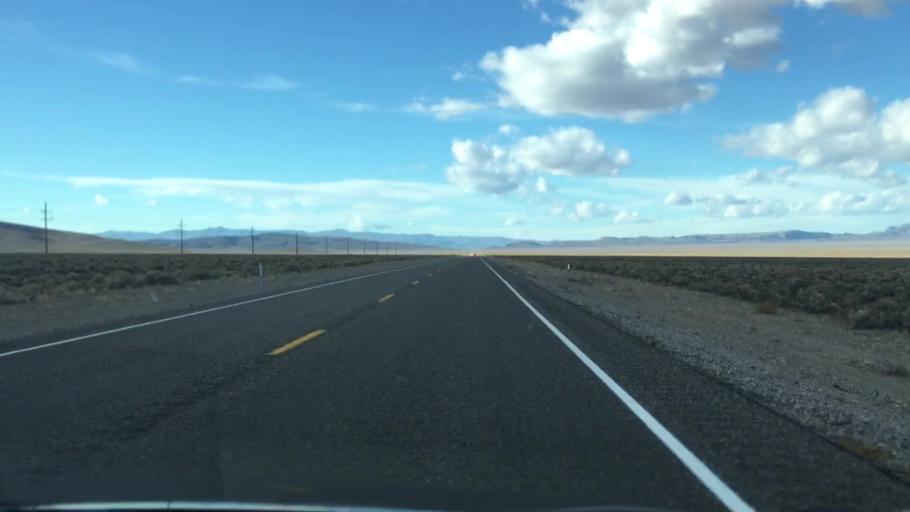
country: US
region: Nevada
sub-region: Nye County
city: Beatty
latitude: 37.1205
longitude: -116.8230
